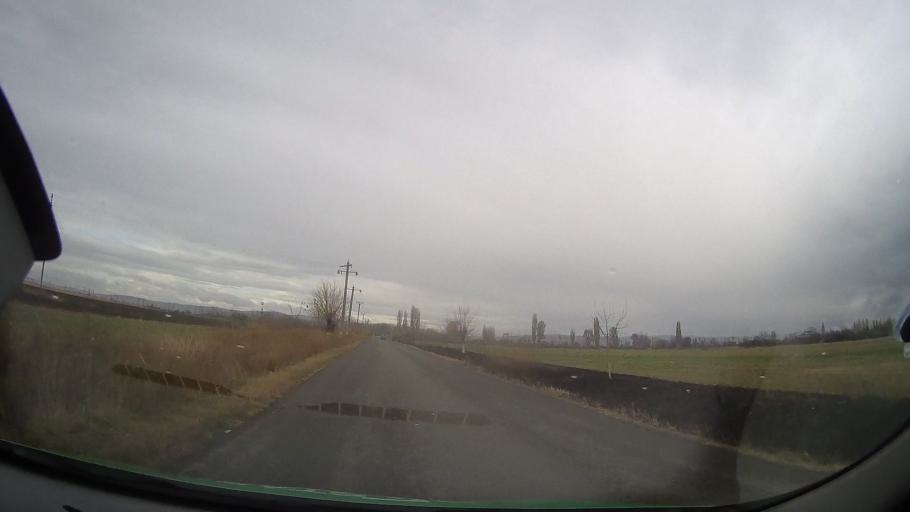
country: RO
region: Prahova
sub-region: Comuna Colceag
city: Inotesti
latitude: 44.9666
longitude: 26.3459
